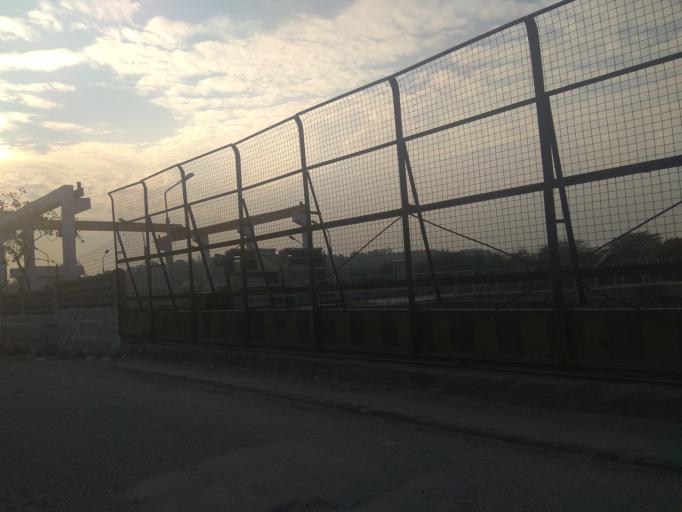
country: IN
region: NCT
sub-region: West Delhi
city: Nangloi Jat
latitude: 28.6388
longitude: 77.0602
